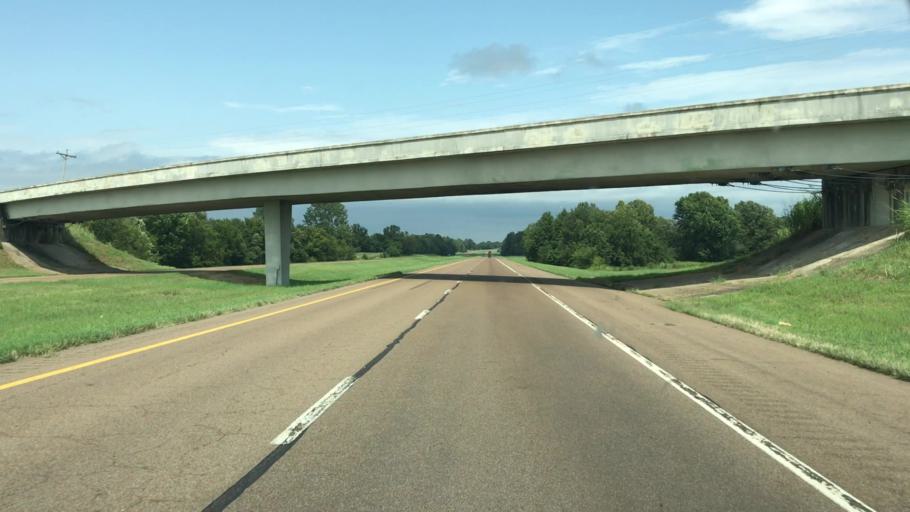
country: US
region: Tennessee
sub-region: Obion County
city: Union City
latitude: 36.4658
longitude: -88.9755
